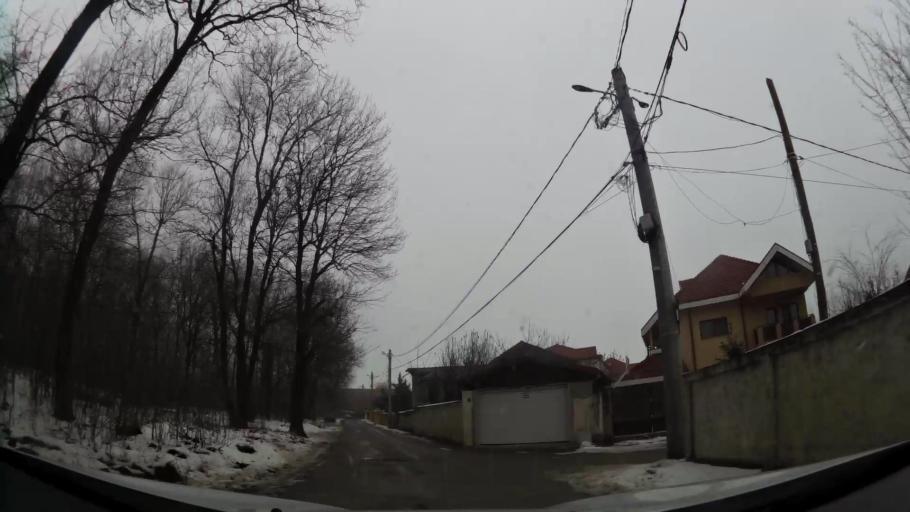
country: RO
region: Ilfov
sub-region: Comuna Chiajna
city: Rosu
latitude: 44.4559
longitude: 26.0043
